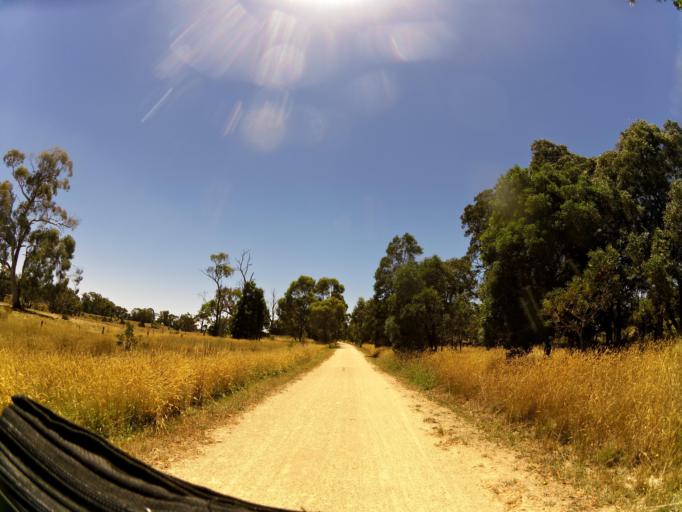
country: AU
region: Victoria
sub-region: Ballarat North
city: Delacombe
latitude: -37.6161
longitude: 143.7104
